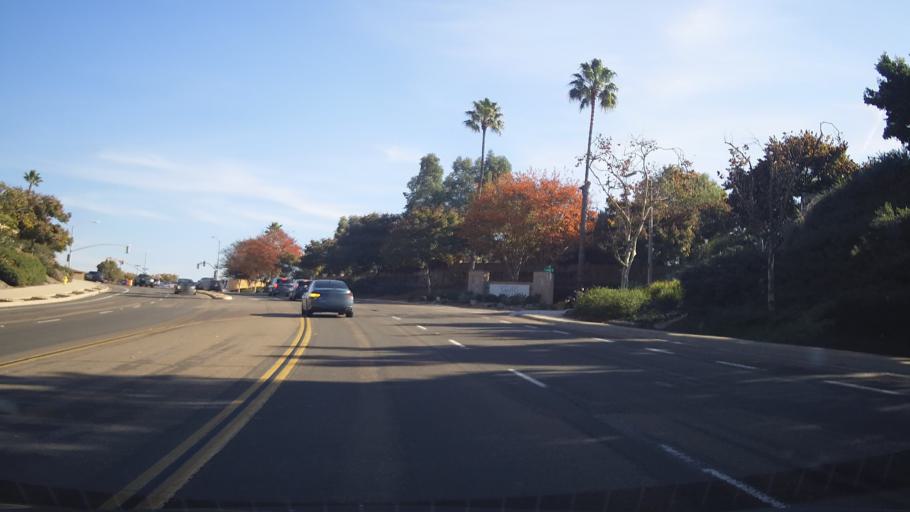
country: US
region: California
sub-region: San Diego County
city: La Mesa
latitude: 32.8099
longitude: -117.1074
